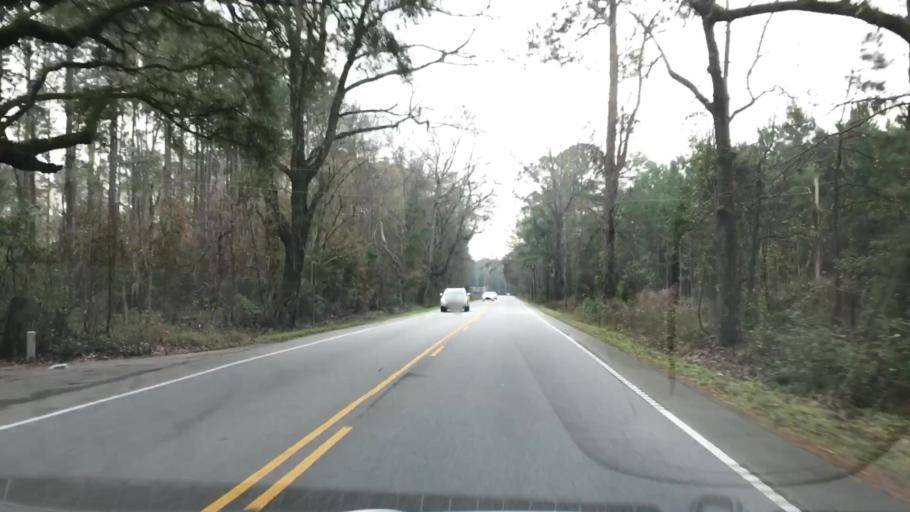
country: US
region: South Carolina
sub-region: Jasper County
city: Ridgeland
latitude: 32.5667
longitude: -80.9171
